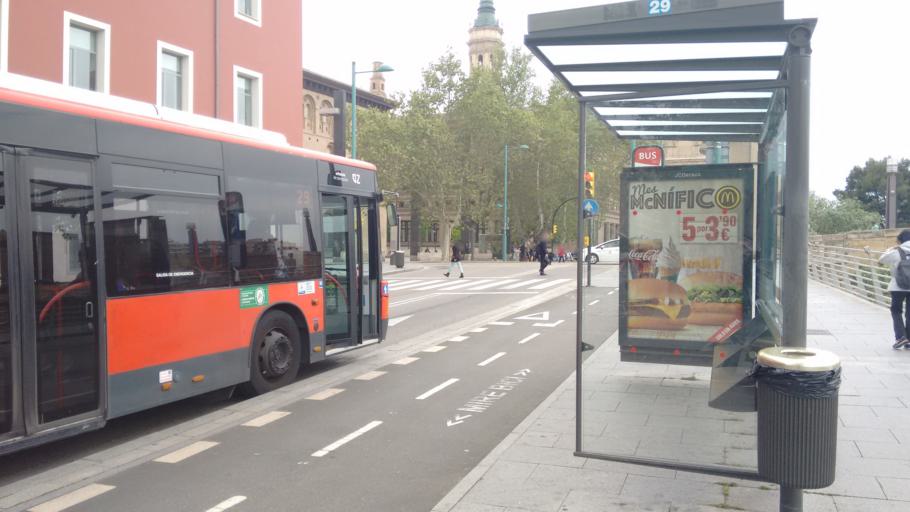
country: ES
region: Aragon
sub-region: Provincia de Zaragoza
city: Zaragoza
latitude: 41.6559
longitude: -0.8754
